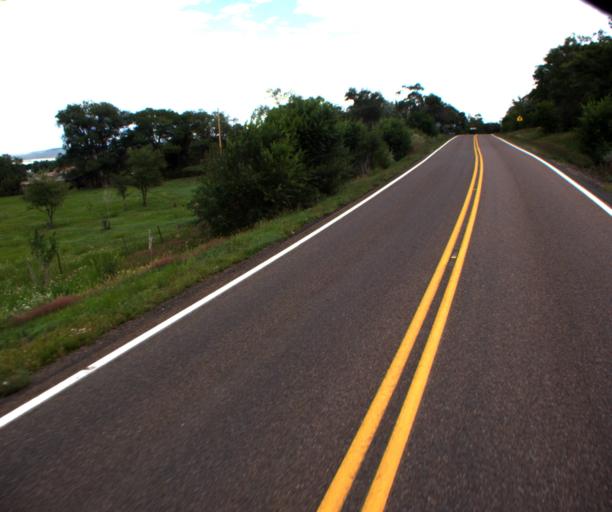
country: US
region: Arizona
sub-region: Apache County
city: Eagar
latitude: 34.1105
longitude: -109.3032
